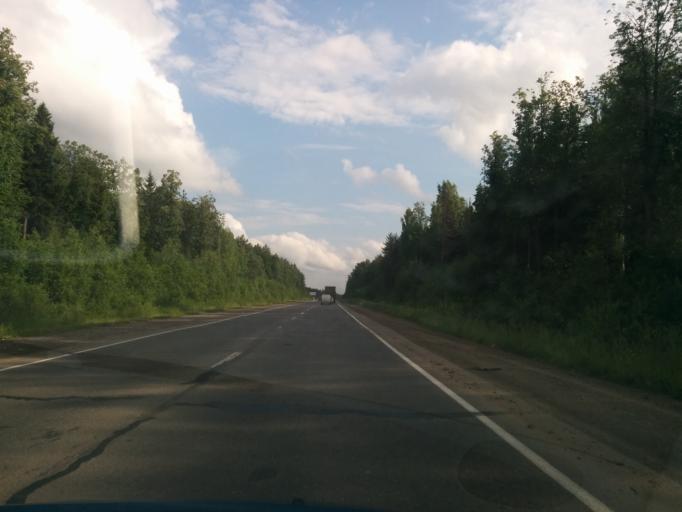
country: RU
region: Perm
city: Polazna
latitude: 58.1227
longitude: 56.4240
